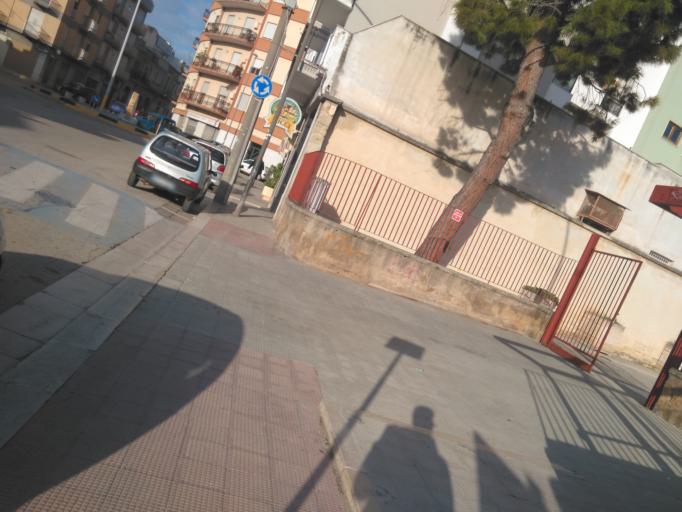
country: IT
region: Apulia
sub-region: Provincia di Barletta - Andria - Trani
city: Andria
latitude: 41.2205
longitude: 16.2976
